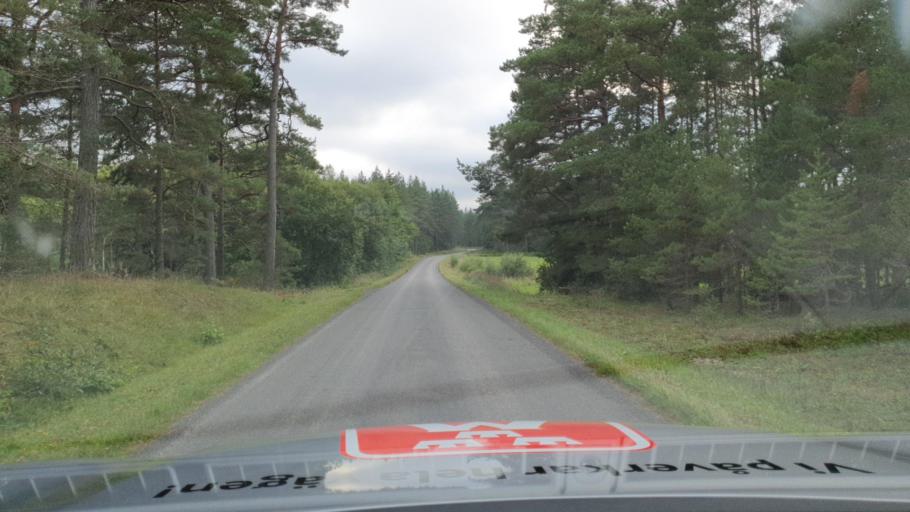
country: SE
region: Gotland
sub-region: Gotland
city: Vibble
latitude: 57.5055
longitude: 18.2700
